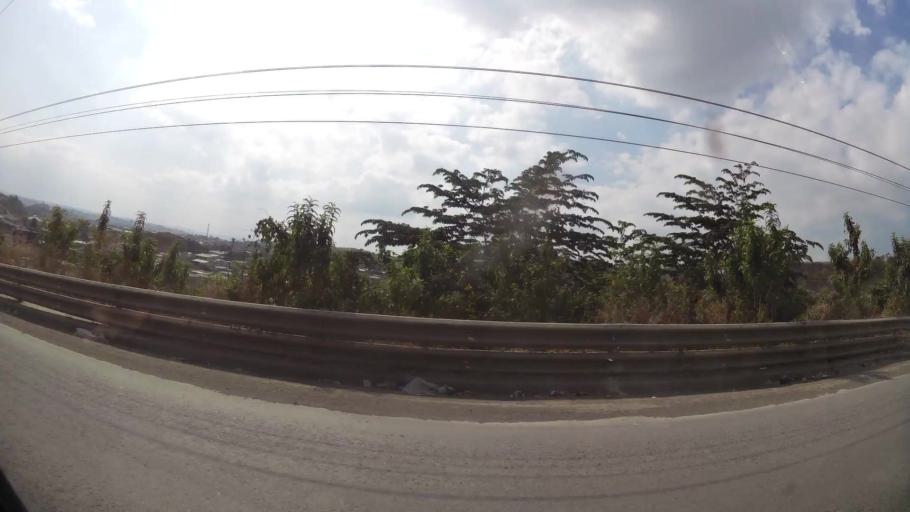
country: EC
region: Guayas
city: Santa Lucia
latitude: -2.1204
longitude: -79.9761
